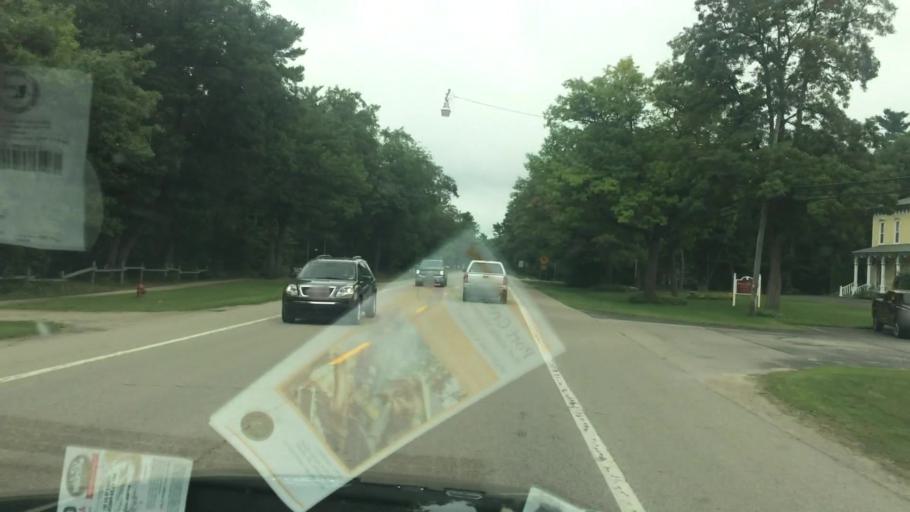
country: US
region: Michigan
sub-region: Huron County
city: Pigeon
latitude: 43.9525
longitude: -83.2673
